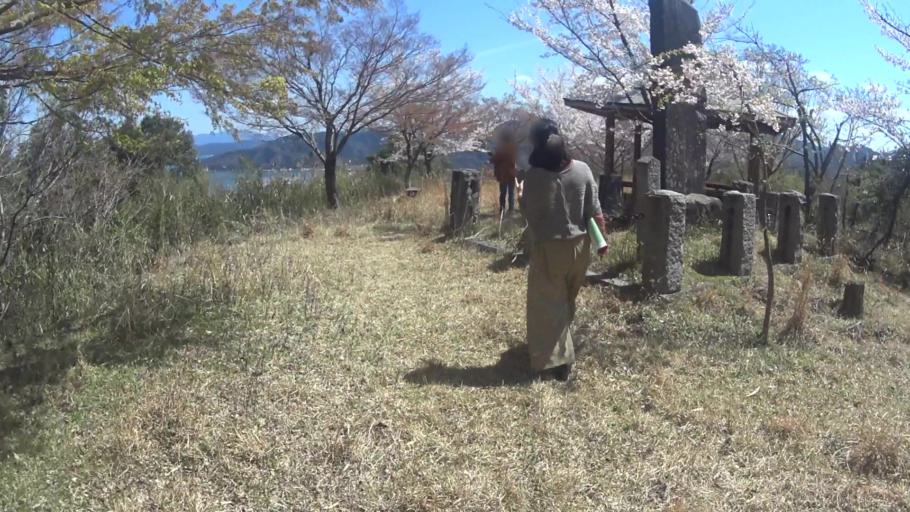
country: JP
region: Kyoto
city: Miyazu
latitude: 35.5643
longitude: 135.1376
